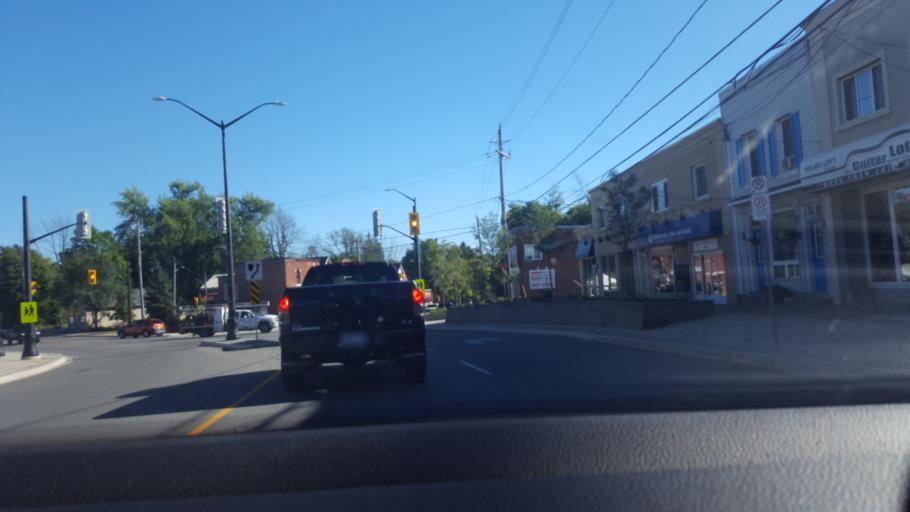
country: CA
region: Ontario
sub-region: Regional Municipality of Niagara
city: St. Catharines
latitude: 43.0986
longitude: -79.5465
